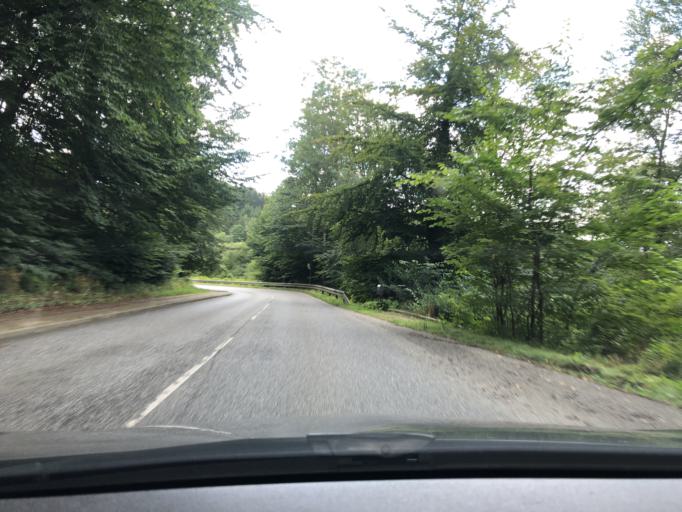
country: DK
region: South Denmark
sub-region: Vejle Kommune
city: Vejle
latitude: 55.7587
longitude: 9.5339
